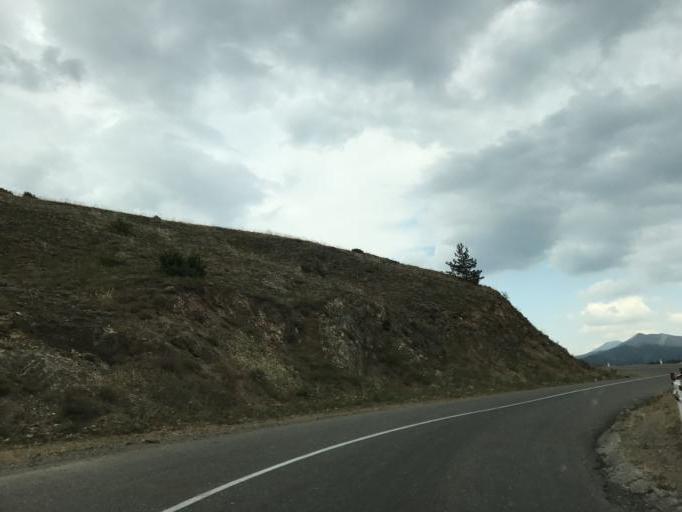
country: AZ
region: Susa
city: Shushi
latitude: 39.7186
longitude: 46.6698
